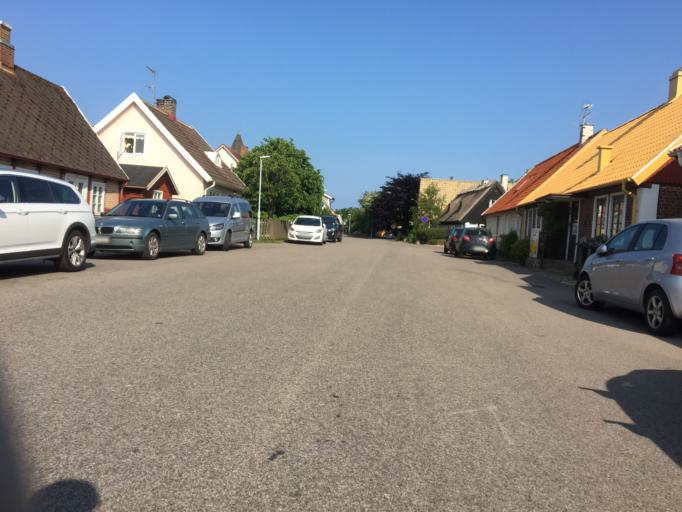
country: SE
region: Skane
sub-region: Hoganas Kommun
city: Hoganas
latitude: 56.1454
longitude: 12.5740
